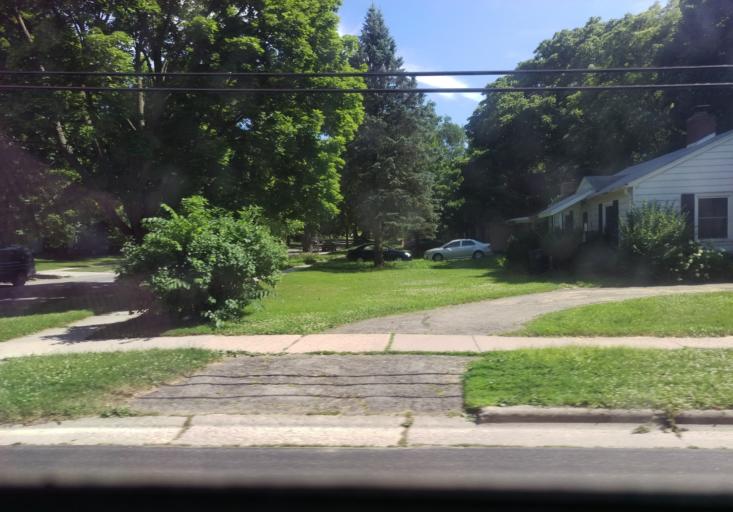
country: US
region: Wisconsin
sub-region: Dane County
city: Shorewood Hills
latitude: 43.0680
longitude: -89.4476
